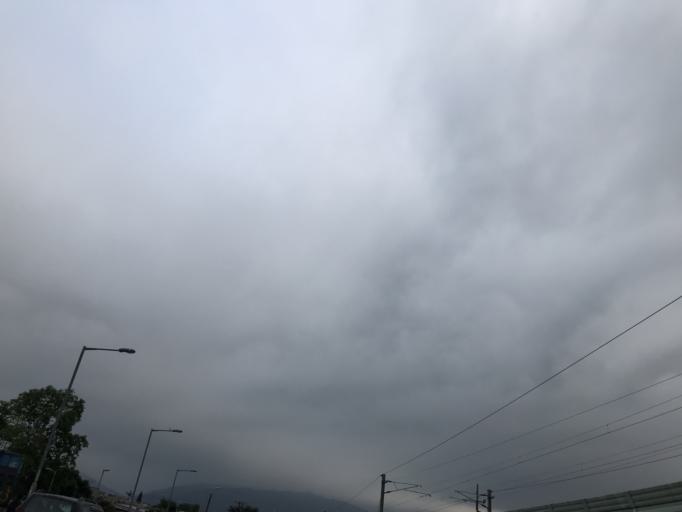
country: HK
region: Tai Po
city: Tai Po
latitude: 22.4784
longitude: 114.1551
